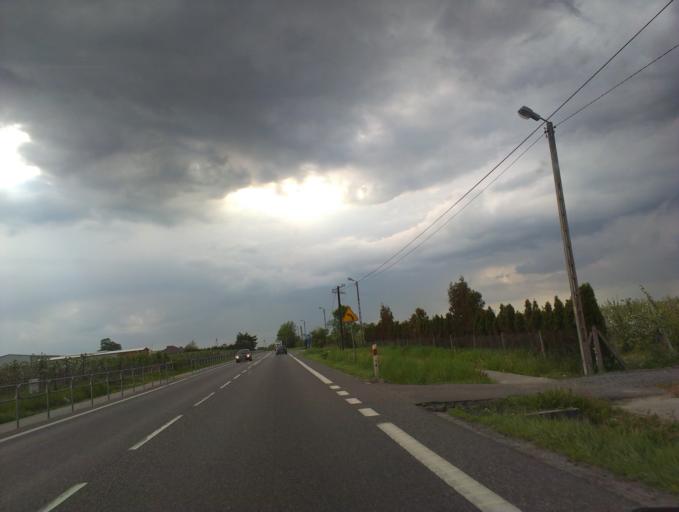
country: PL
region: Masovian Voivodeship
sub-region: Powiat grojecki
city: Pniewy
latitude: 51.9122
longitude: 20.7260
